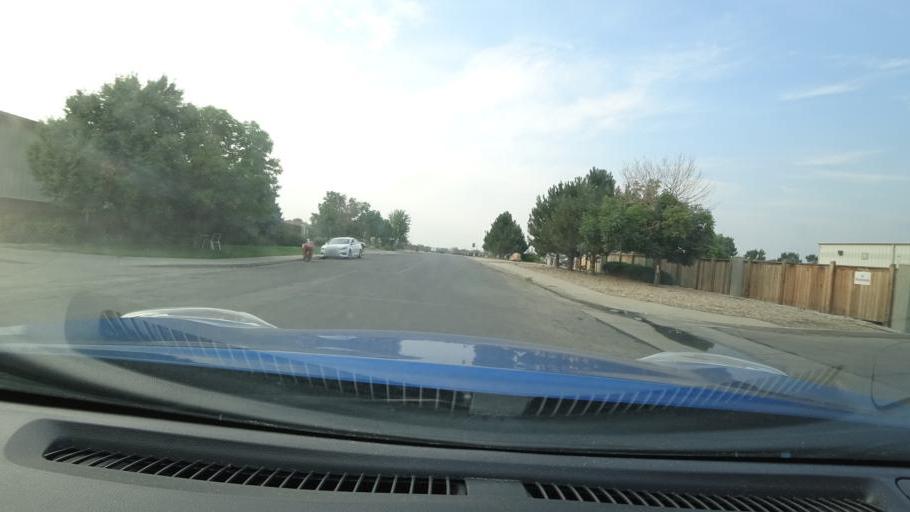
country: US
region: Colorado
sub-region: Adams County
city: Aurora
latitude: 39.7319
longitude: -104.7832
